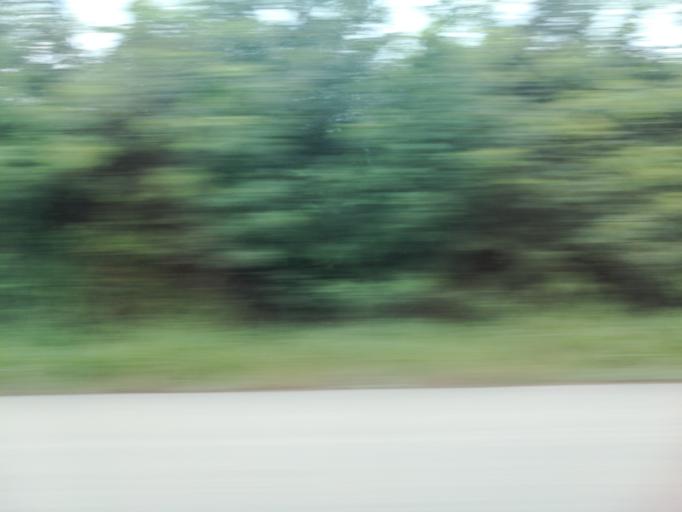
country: TH
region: Prachuap Khiri Khan
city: Sam Roi Yot
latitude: 12.2982
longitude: 99.8748
